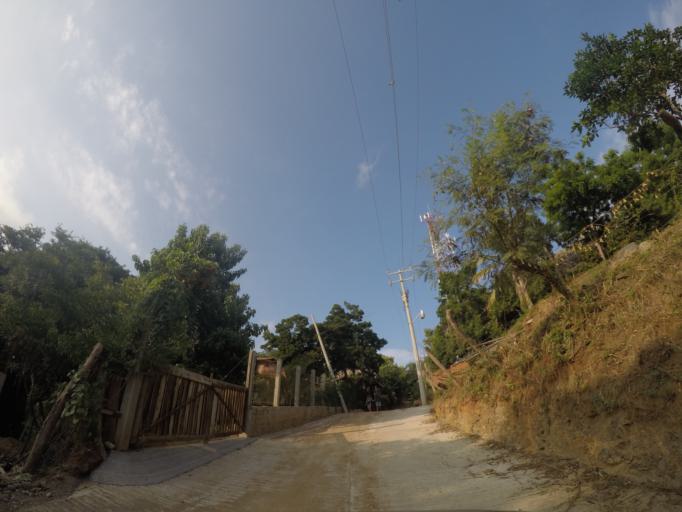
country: MX
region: Oaxaca
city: Santa Maria Tonameca
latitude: 15.6673
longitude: -96.5480
